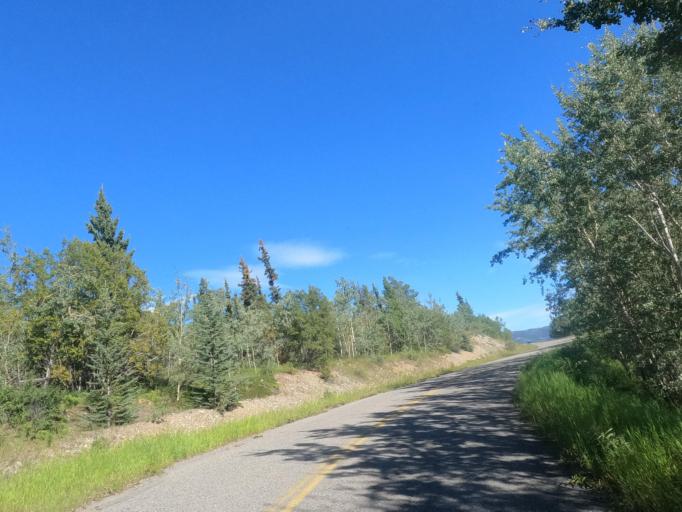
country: CA
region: Yukon
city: Whitehorse
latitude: 60.6670
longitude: -135.0356
